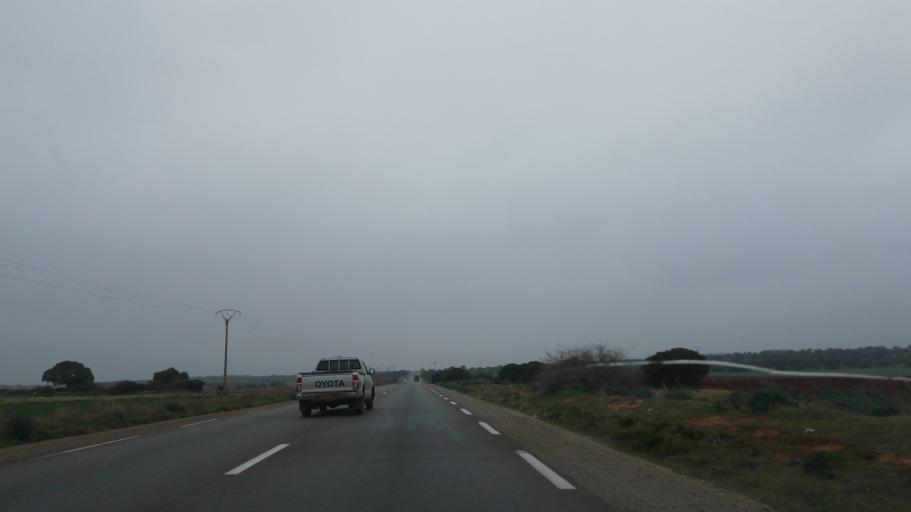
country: DZ
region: Mascara
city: Mascara
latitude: 35.3068
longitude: 0.4219
